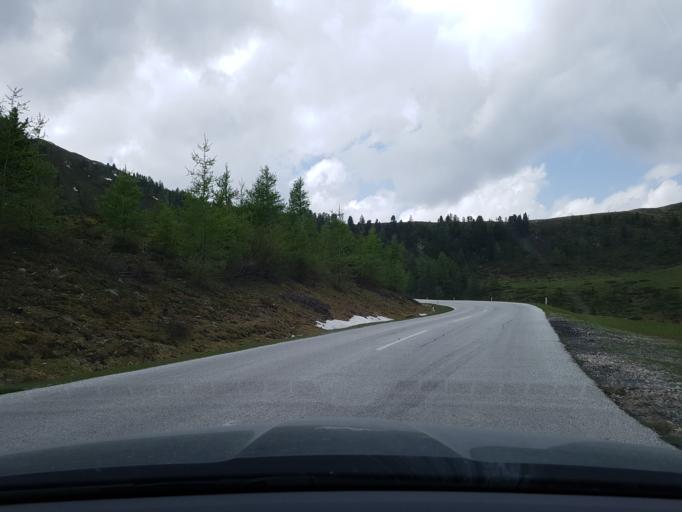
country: AT
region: Carinthia
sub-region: Politischer Bezirk Spittal an der Drau
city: Kleinkirchheim
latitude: 46.8956
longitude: 13.7901
